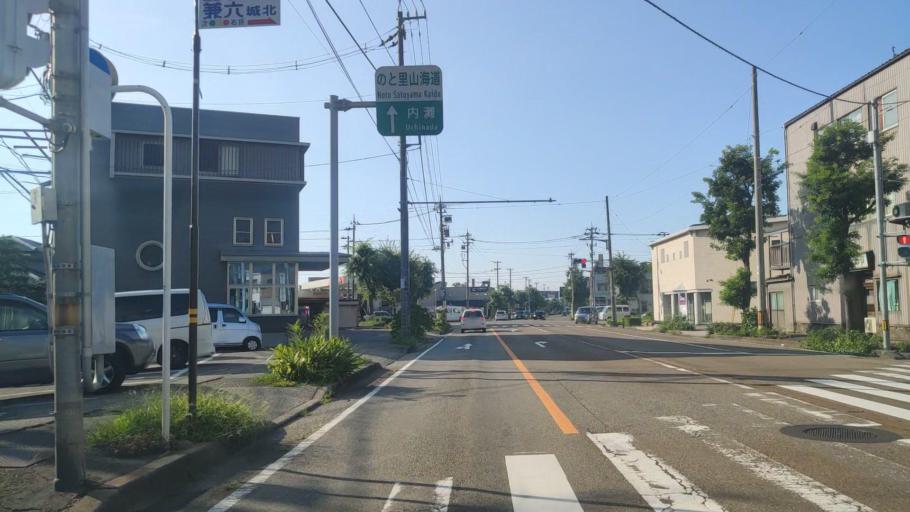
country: JP
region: Ishikawa
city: Kanazawa-shi
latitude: 36.5775
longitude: 136.6647
